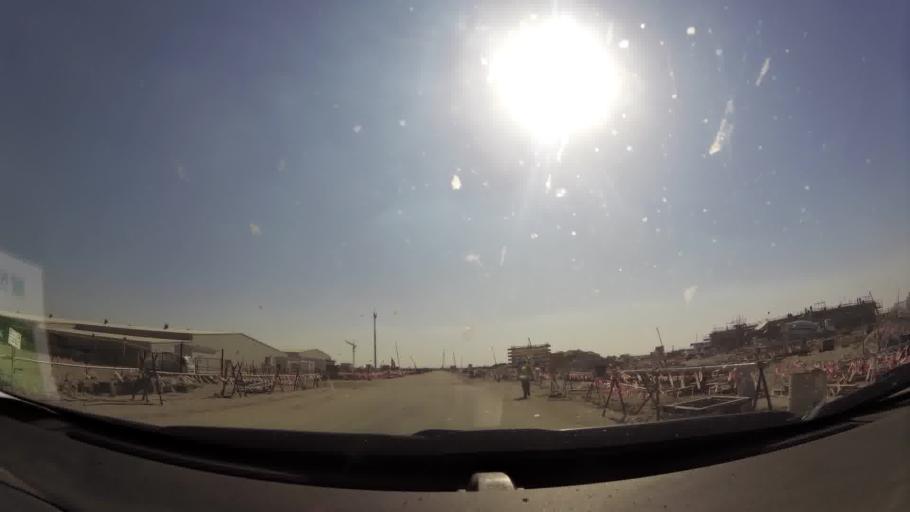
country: SA
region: Eastern Province
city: Al Khafji
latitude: 28.7071
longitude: 48.3404
